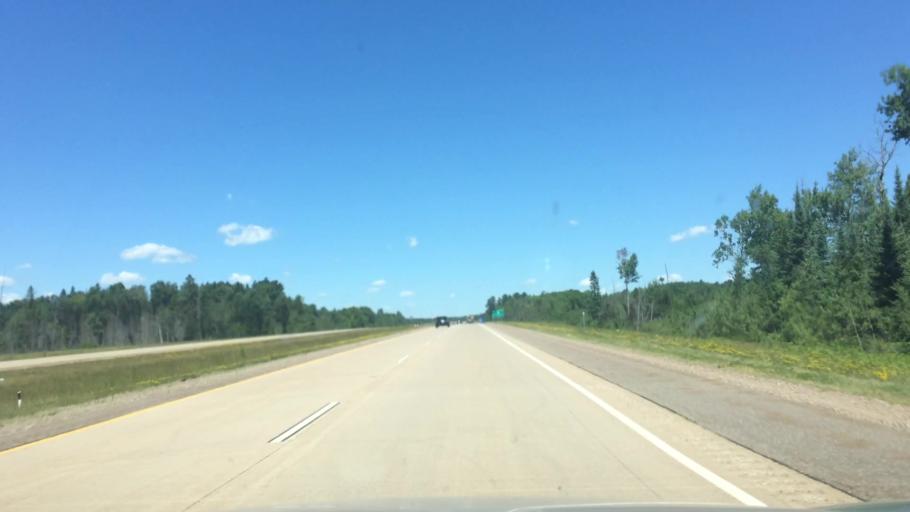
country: US
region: Wisconsin
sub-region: Lincoln County
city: Tomahawk
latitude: 45.4019
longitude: -89.6719
